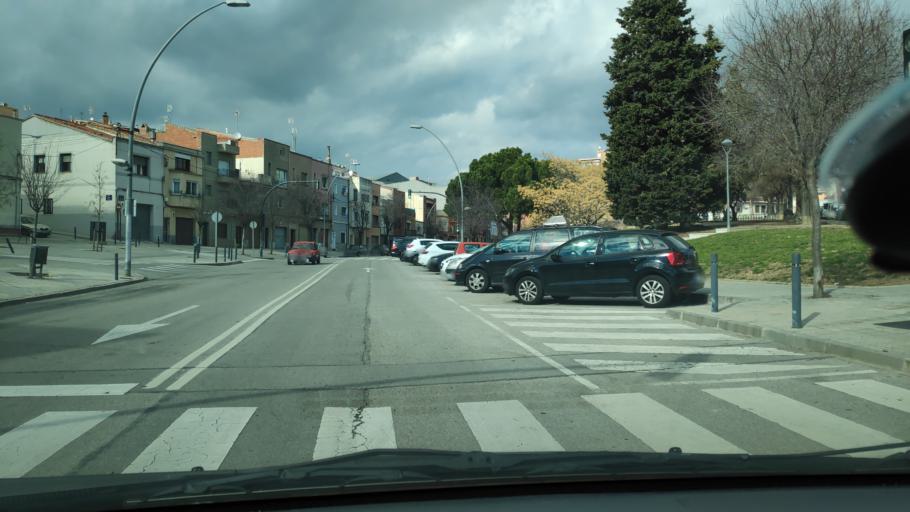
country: ES
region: Catalonia
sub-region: Provincia de Barcelona
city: Terrassa
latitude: 41.5615
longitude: 1.9984
